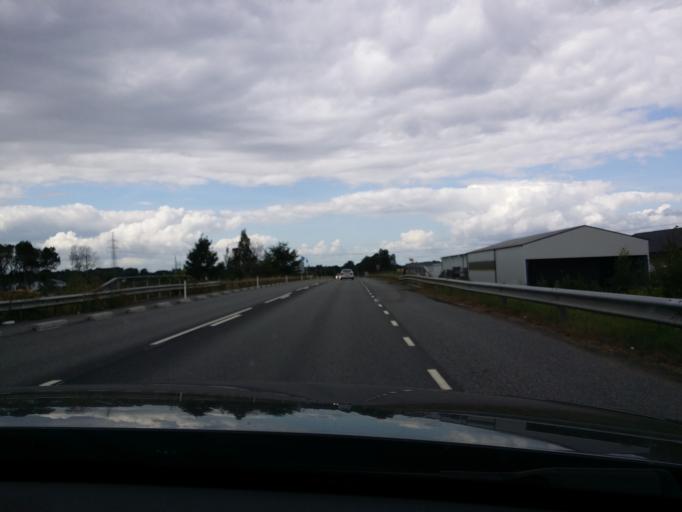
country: SE
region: Skane
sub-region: Bromolla Kommun
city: Bromoella
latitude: 56.0646
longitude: 14.4947
